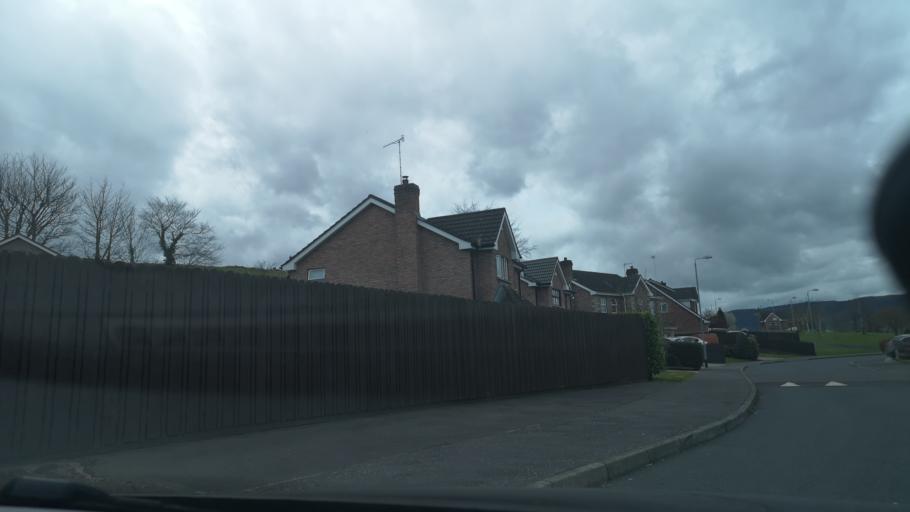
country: GB
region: Northern Ireland
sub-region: Newry and Mourne District
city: Newry
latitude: 54.1830
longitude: -6.3221
